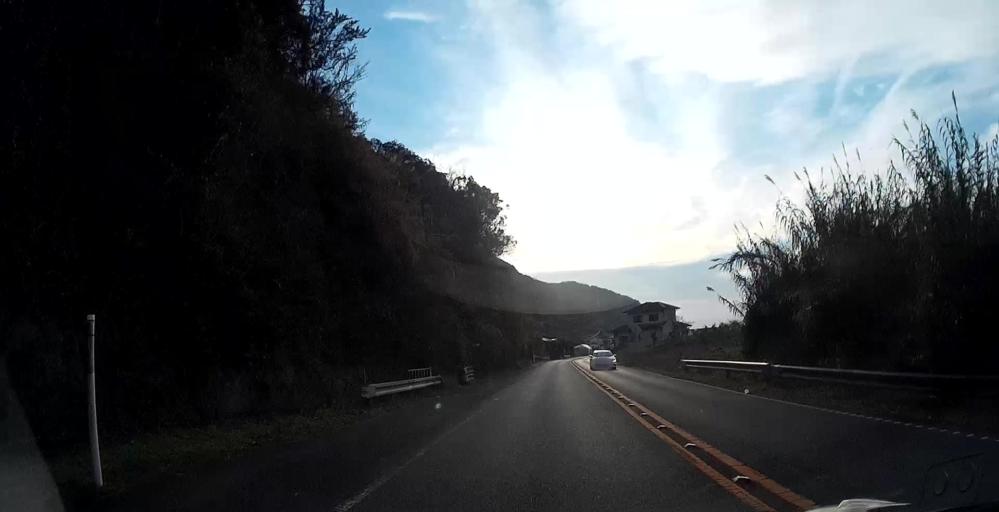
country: JP
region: Kumamoto
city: Matsubase
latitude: 32.6499
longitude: 130.4949
